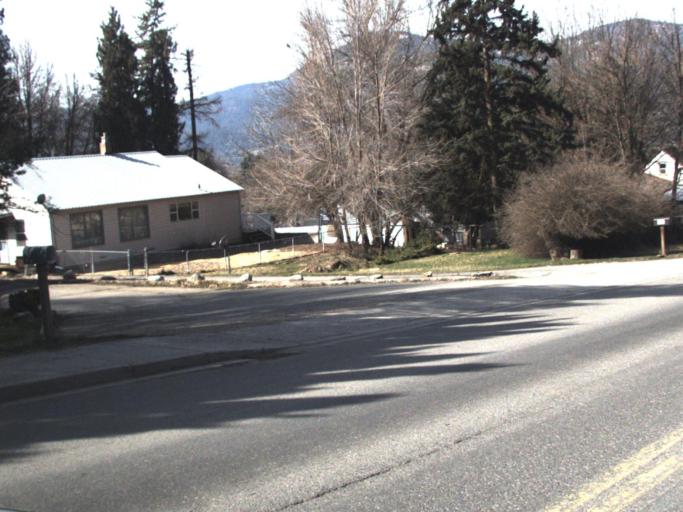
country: US
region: Washington
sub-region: Stevens County
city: Colville
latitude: 48.5466
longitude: -117.8957
